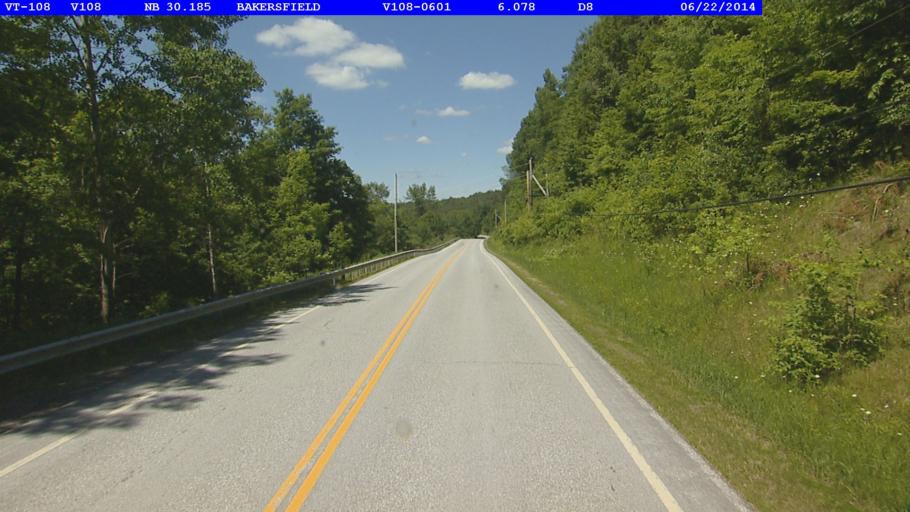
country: US
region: Vermont
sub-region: Franklin County
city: Enosburg Falls
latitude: 44.8138
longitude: -72.7903
